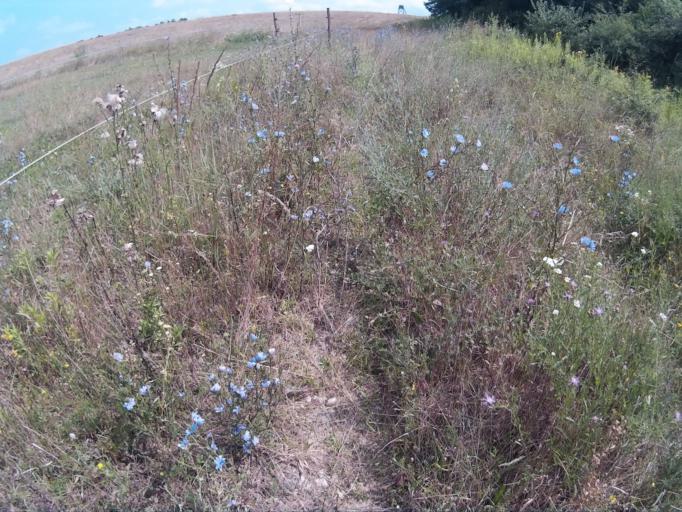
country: HU
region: Veszprem
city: Papa
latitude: 47.2902
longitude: 17.6118
